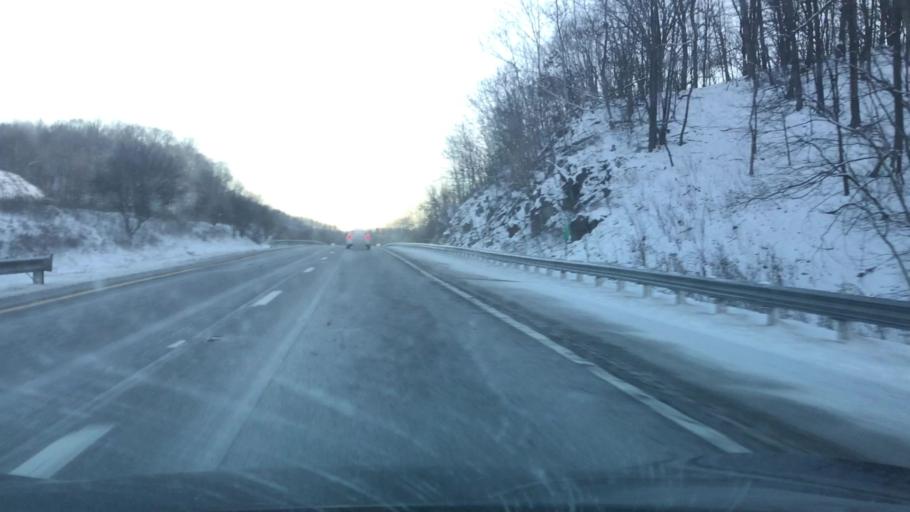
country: US
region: Virginia
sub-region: Montgomery County
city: Shawsville
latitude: 37.1982
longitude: -80.2680
